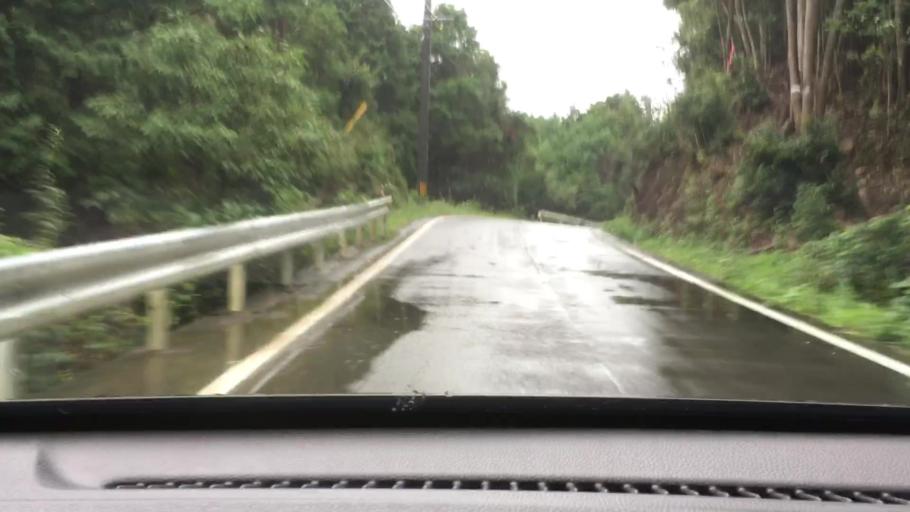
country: JP
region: Nagasaki
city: Togitsu
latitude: 32.8724
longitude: 129.7644
